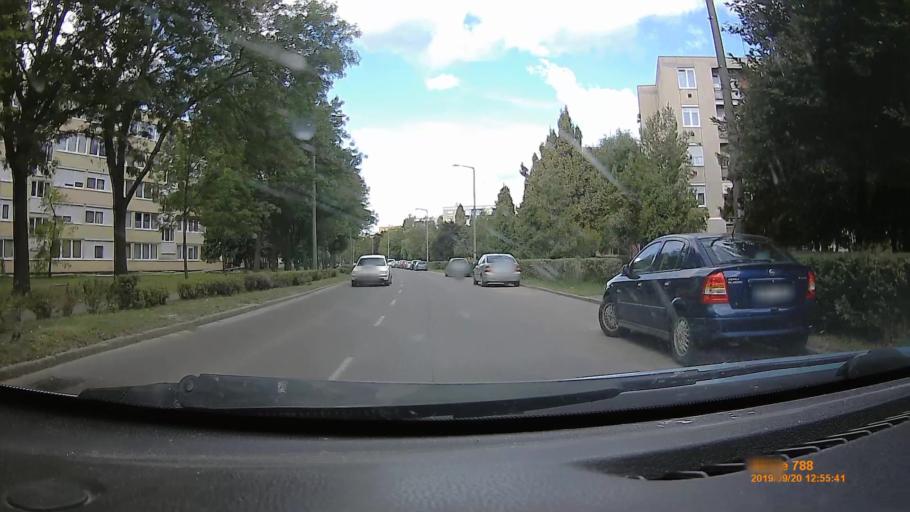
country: HU
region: Heves
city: Eger
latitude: 47.9181
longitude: 20.3755
